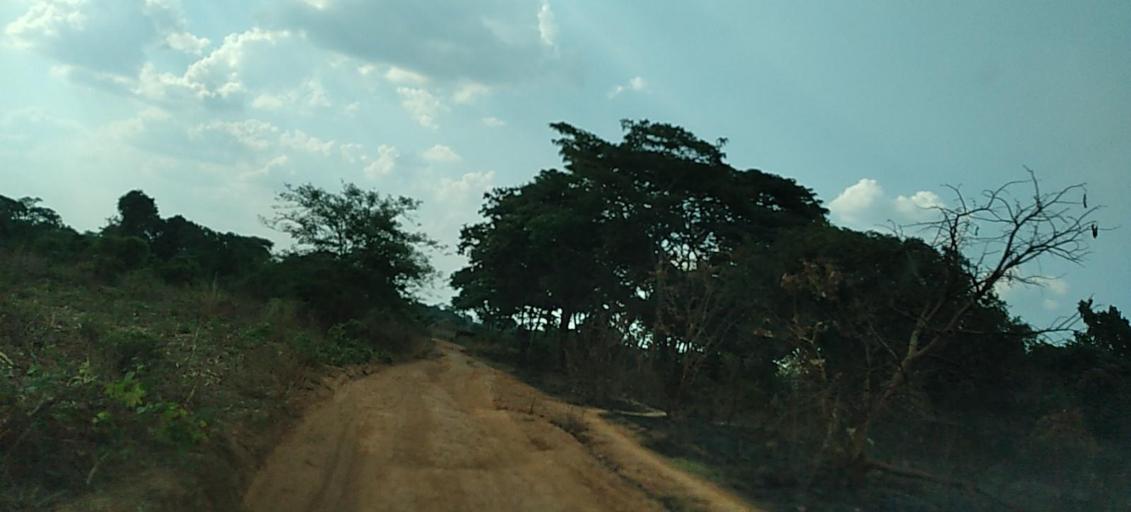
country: ZM
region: Copperbelt
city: Mpongwe
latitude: -13.5131
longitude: 28.0976
